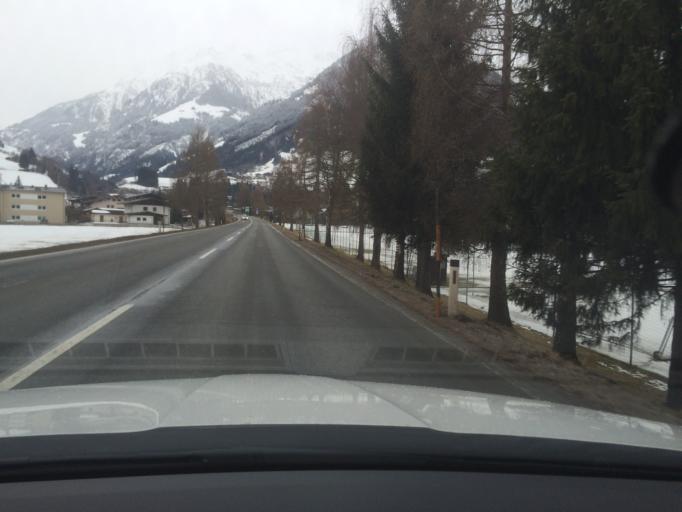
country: AT
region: Salzburg
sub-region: Politischer Bezirk Zell am See
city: Mittersill
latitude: 47.2809
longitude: 12.4897
